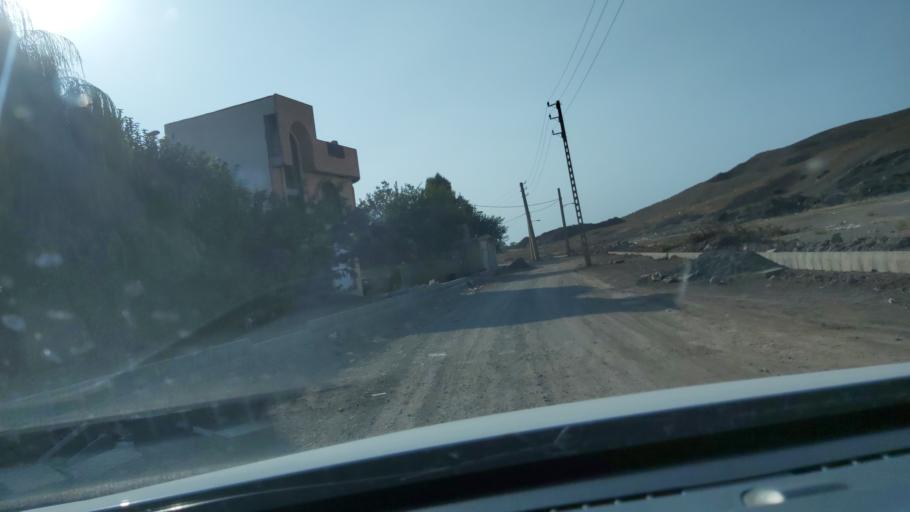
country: IR
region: Alborz
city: Hashtgerd
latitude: 35.9538
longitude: 50.7879
